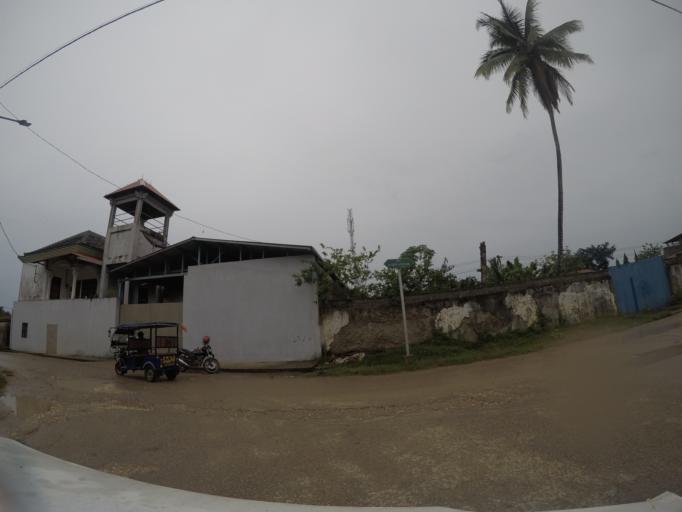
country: TL
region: Lautem
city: Lospalos
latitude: -8.5235
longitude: 126.9973
